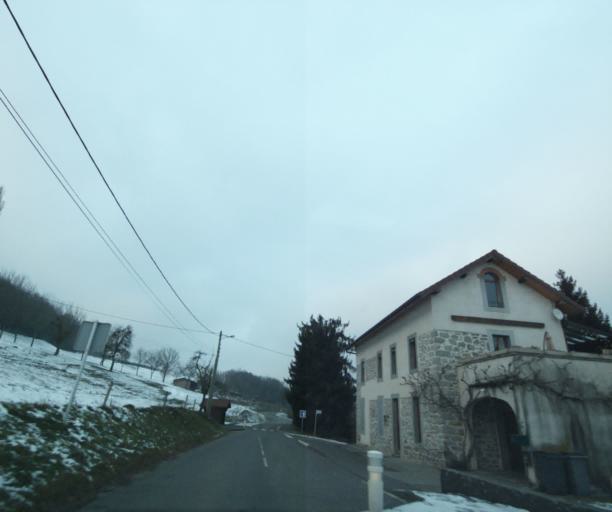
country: FR
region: Rhone-Alpes
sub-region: Departement de la Haute-Savoie
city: Arthaz-Pont-Notre-Dame
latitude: 46.1505
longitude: 6.2453
